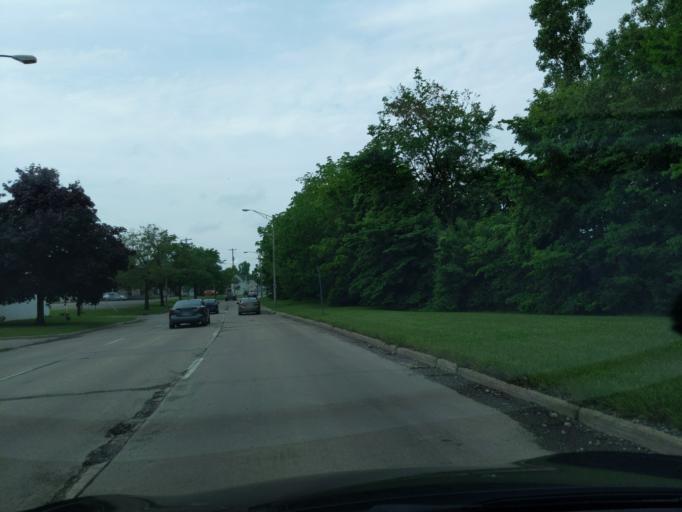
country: US
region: Michigan
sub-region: Ingham County
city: Lansing
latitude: 42.7416
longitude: -84.5506
